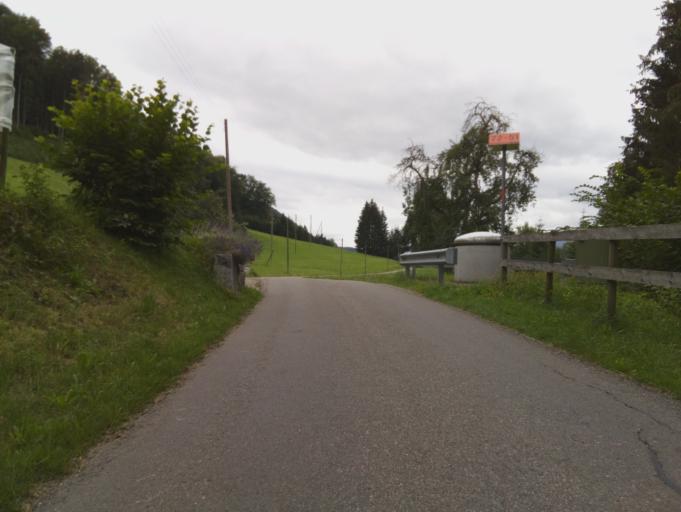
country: CH
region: Saint Gallen
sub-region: Wahlkreis Toggenburg
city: Ganterschwil
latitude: 47.3739
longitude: 9.0837
